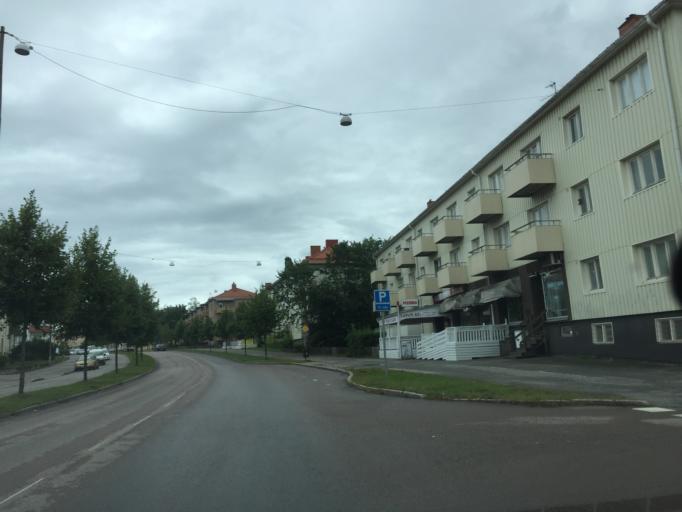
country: SE
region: Soedermanland
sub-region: Eskilstuna Kommun
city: Eskilstuna
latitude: 59.3693
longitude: 16.5331
